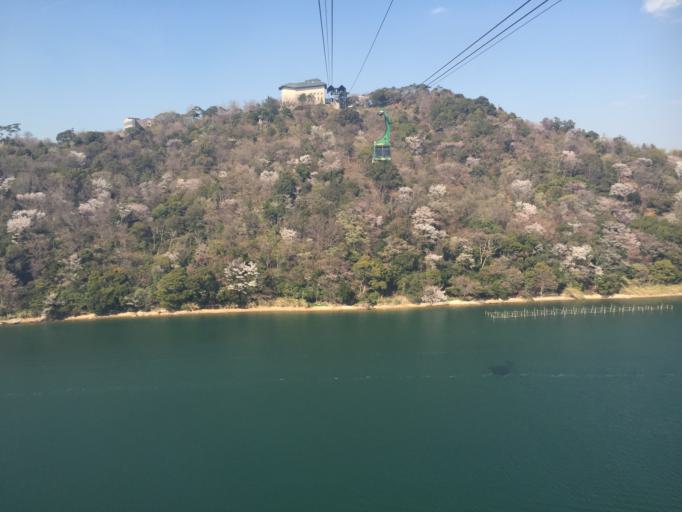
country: JP
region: Shizuoka
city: Kosai-shi
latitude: 34.7665
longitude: 137.6189
